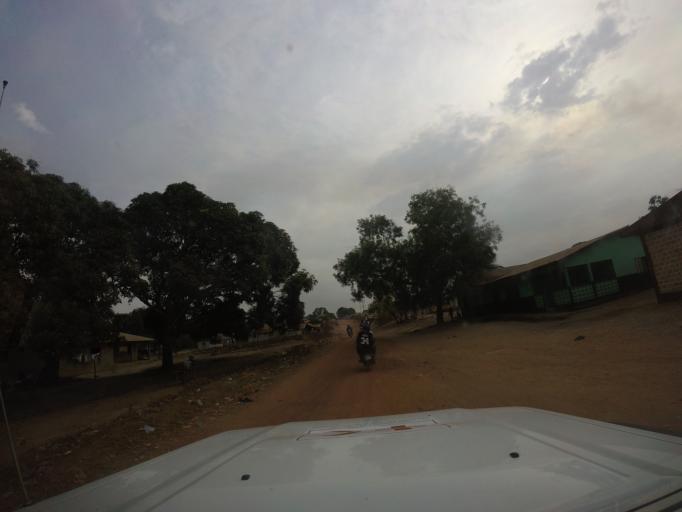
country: LR
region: Grand Cape Mount
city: Robertsport
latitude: 6.9694
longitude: -11.3120
